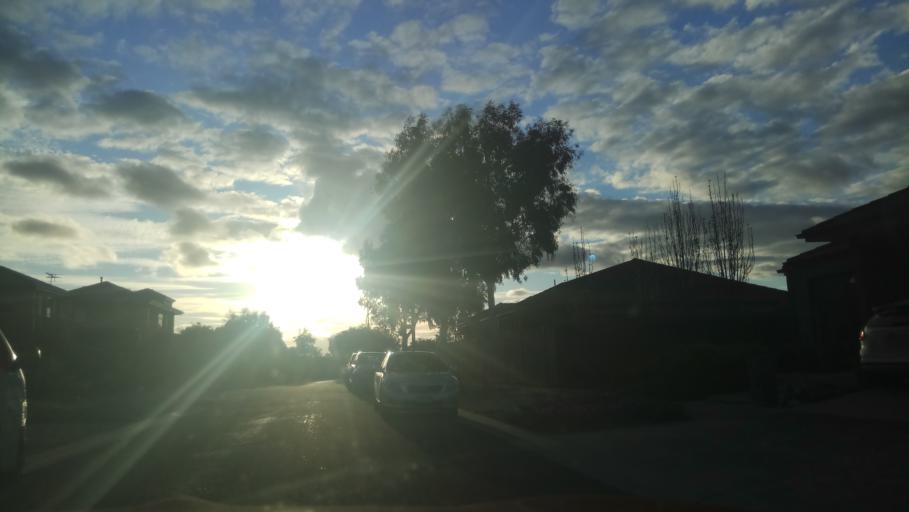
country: AU
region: Victoria
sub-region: Wyndham
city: Point Cook
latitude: -37.9114
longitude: 144.7360
